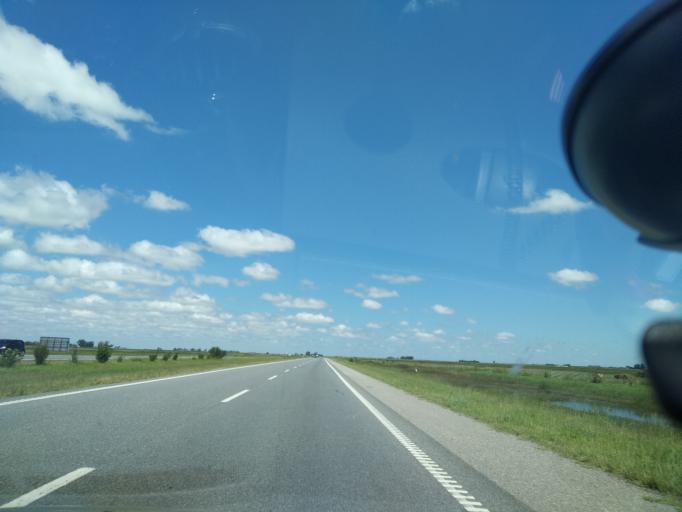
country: AR
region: Cordoba
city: Oliva
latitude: -32.0535
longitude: -63.5071
